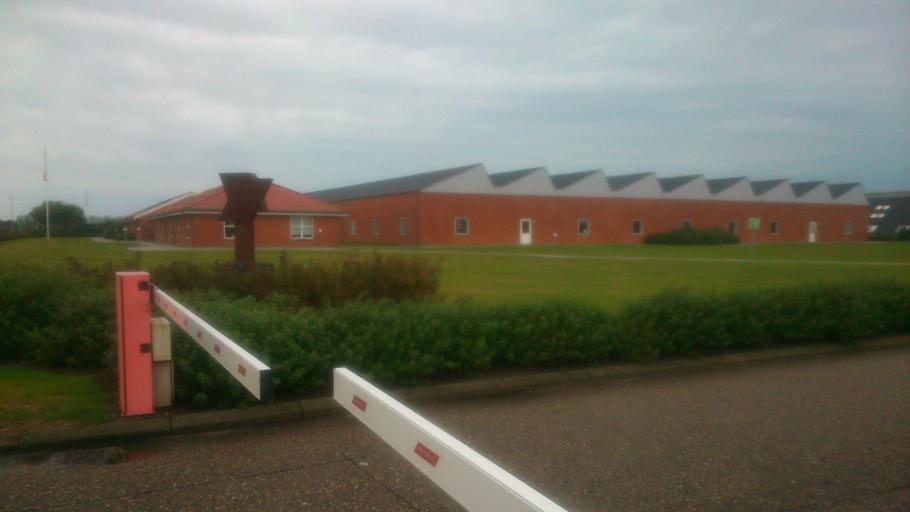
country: DK
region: Central Jutland
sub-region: Ringkobing-Skjern Kommune
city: Skjern
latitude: 55.9602
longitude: 8.5007
